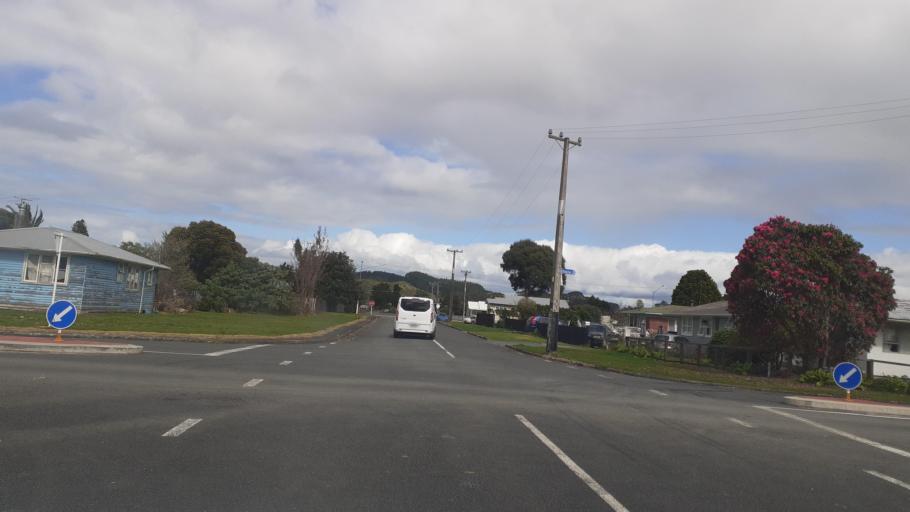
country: NZ
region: Northland
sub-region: Far North District
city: Moerewa
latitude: -35.3877
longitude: 174.0105
